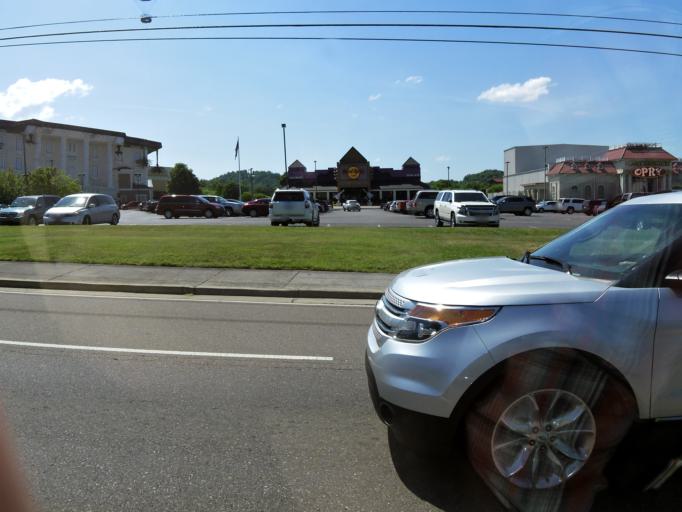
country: US
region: Tennessee
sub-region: Sevier County
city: Pigeon Forge
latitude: 35.8235
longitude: -83.5772
